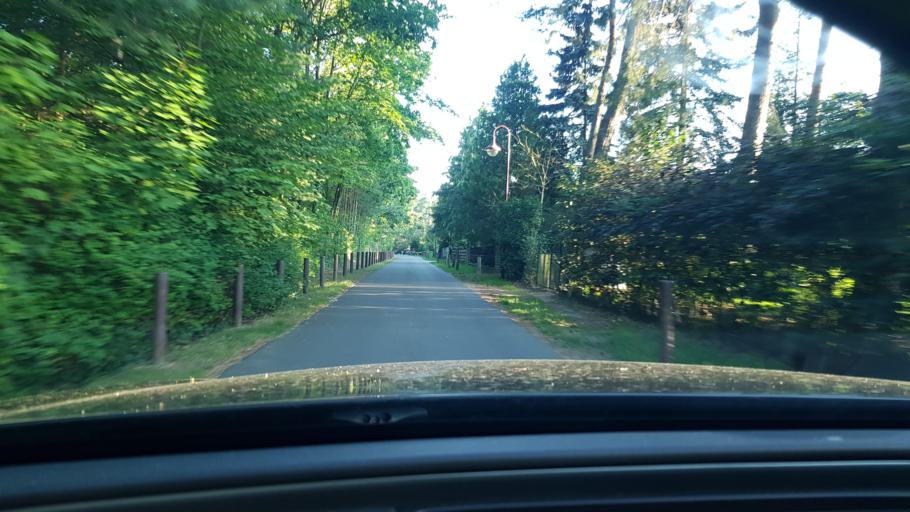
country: DE
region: Brandenburg
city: Neuenhagen
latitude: 52.5146
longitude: 13.7035
